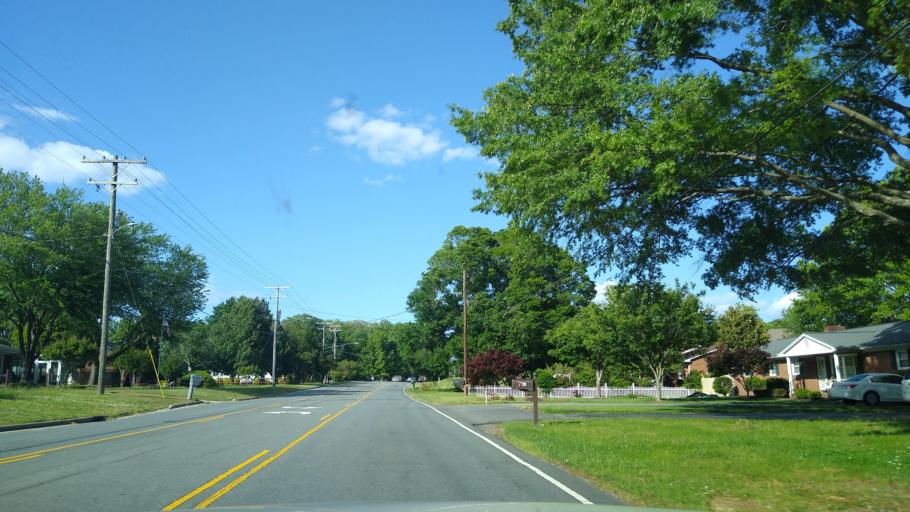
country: US
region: North Carolina
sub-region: Forsyth County
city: Kernersville
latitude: 36.0973
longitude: -80.0859
